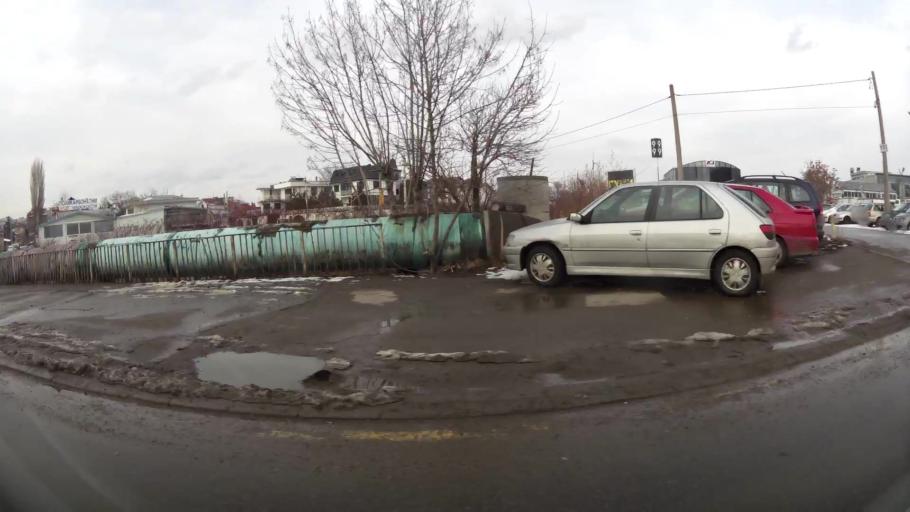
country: BG
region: Sofia-Capital
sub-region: Stolichna Obshtina
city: Sofia
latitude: 42.7113
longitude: 23.3466
